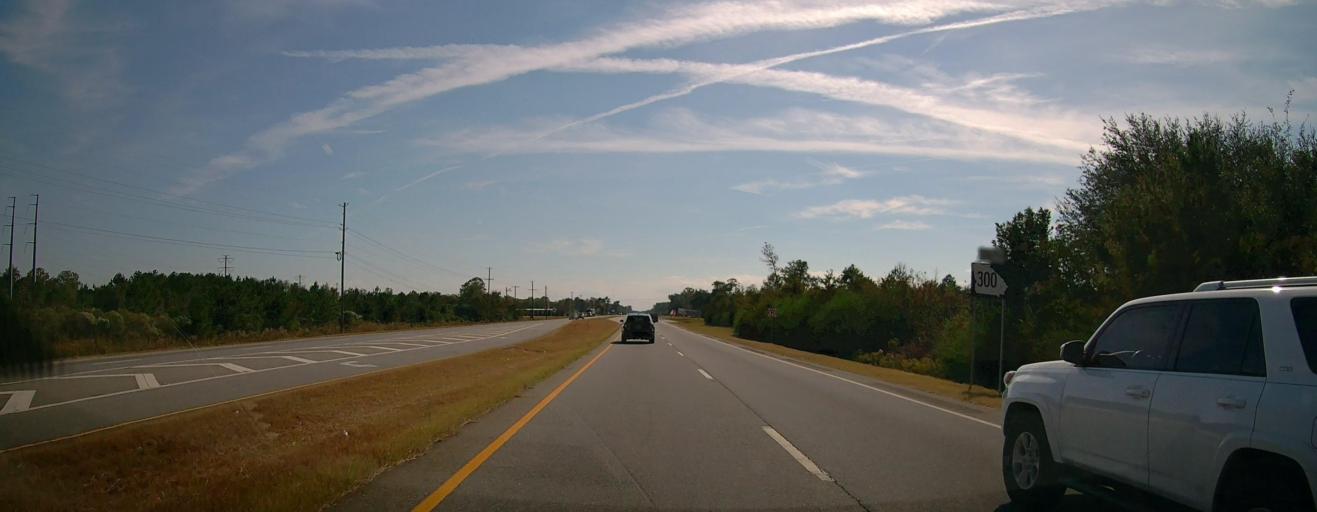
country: US
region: Georgia
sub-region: Dougherty County
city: Putney
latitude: 31.5285
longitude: -84.1157
